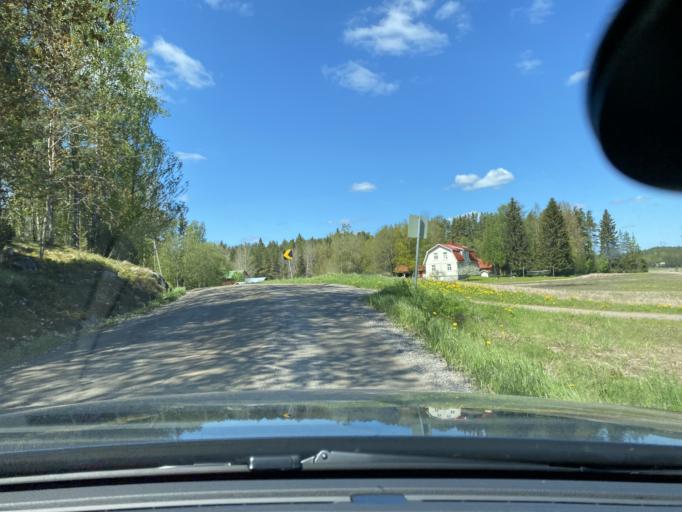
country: FI
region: Varsinais-Suomi
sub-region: Turku
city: Sauvo
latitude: 60.3571
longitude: 22.8742
